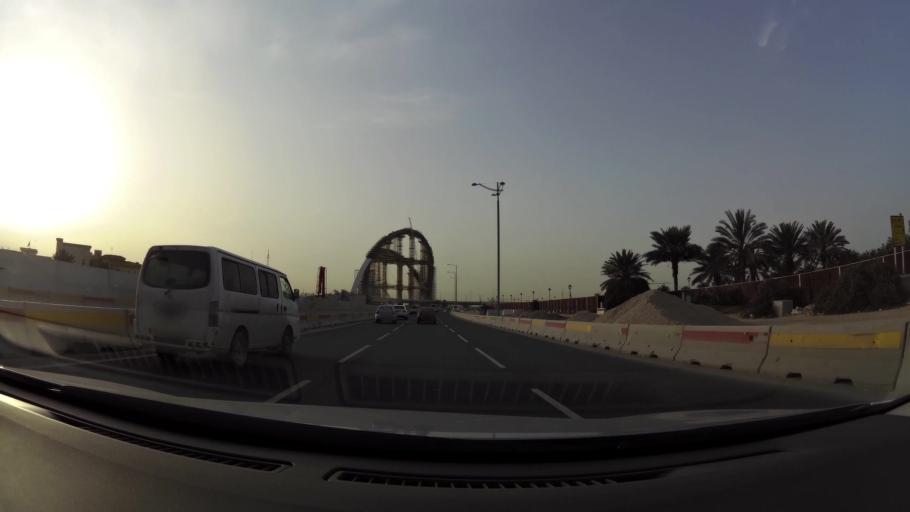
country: QA
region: Baladiyat ad Dawhah
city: Doha
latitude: 25.3321
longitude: 51.5215
